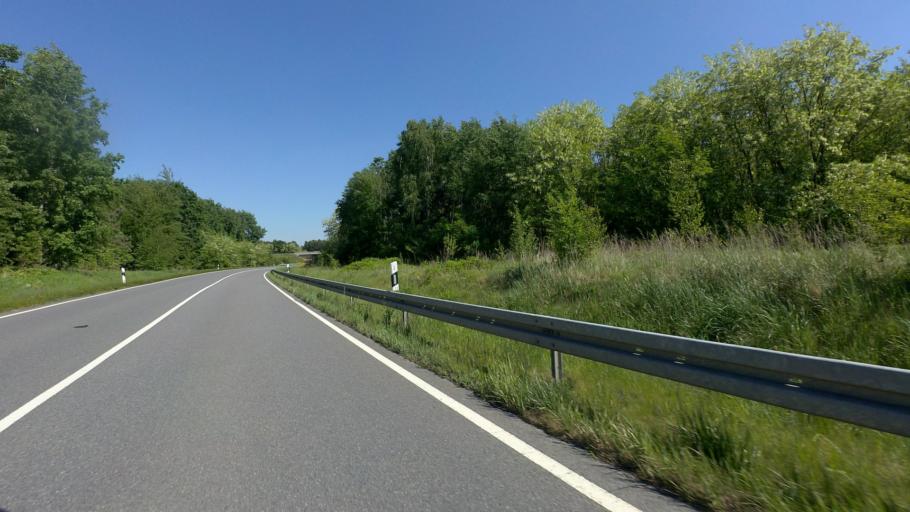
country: DE
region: Brandenburg
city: Spremberg
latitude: 51.5797
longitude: 14.3406
